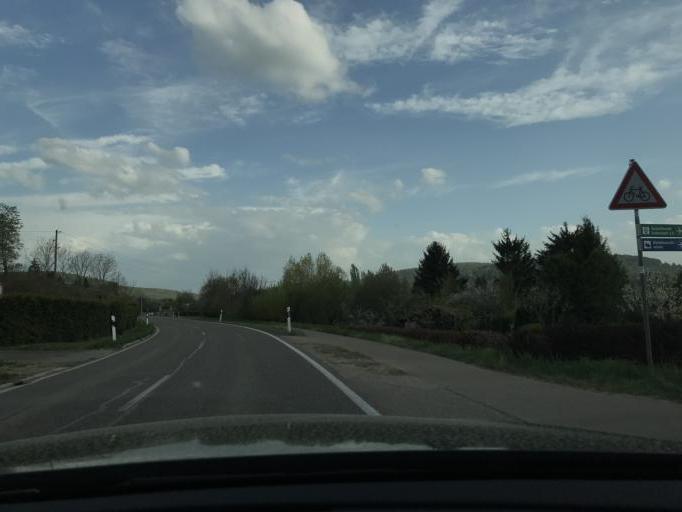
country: DE
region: Baden-Wuerttemberg
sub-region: Regierungsbezirk Stuttgart
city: Weinstadt-Endersbach
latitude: 48.8031
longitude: 9.3507
